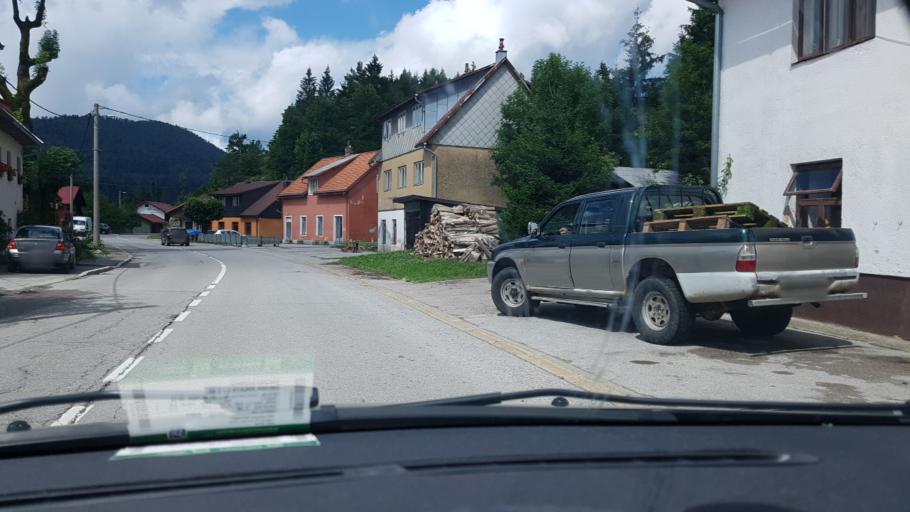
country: HR
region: Primorsko-Goranska
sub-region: Grad Delnice
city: Delnice
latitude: 45.3570
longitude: 14.7479
